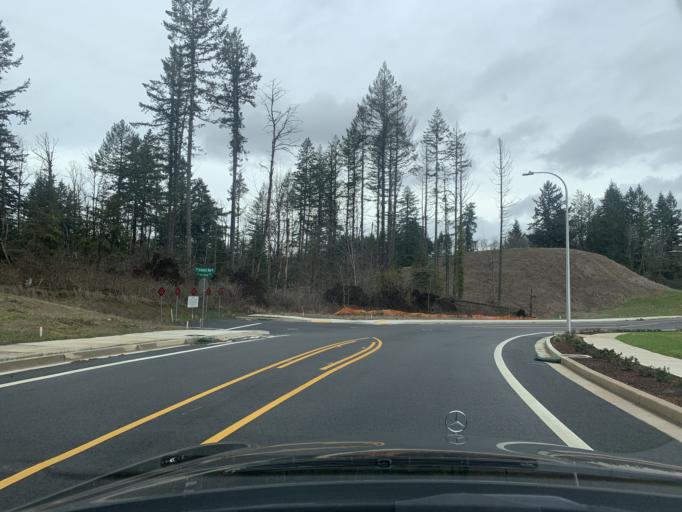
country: US
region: Oregon
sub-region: Clackamas County
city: Happy Valley
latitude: 45.4453
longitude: -122.5043
